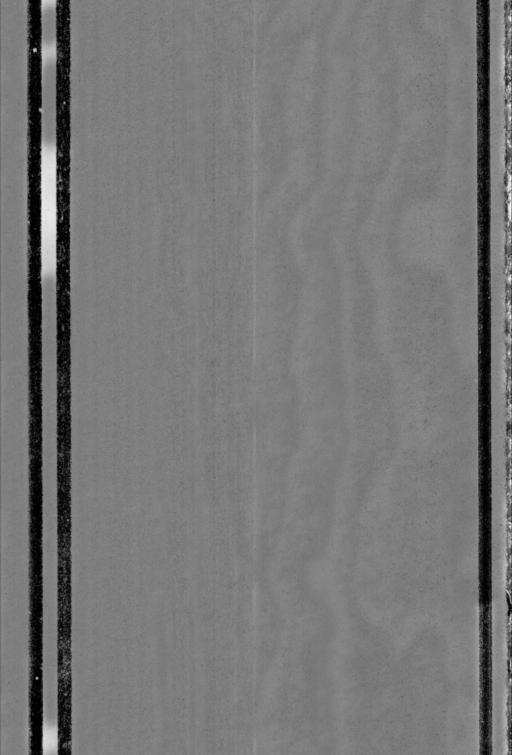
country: US
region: Maryland
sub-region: Prince George's County
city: Coral Hills
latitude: 38.8763
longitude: -76.9518
